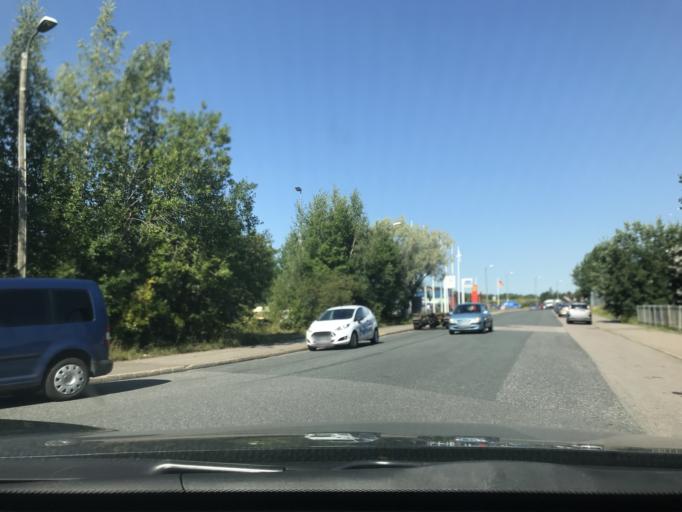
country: FI
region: Uusimaa
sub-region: Helsinki
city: Vantaa
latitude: 60.2432
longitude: 25.0470
